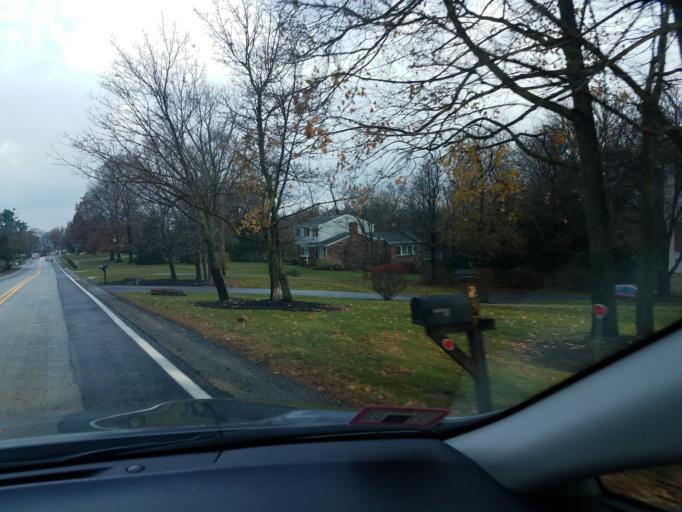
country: US
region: Pennsylvania
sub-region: Allegheny County
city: Franklin Park
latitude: 40.5828
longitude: -80.0873
